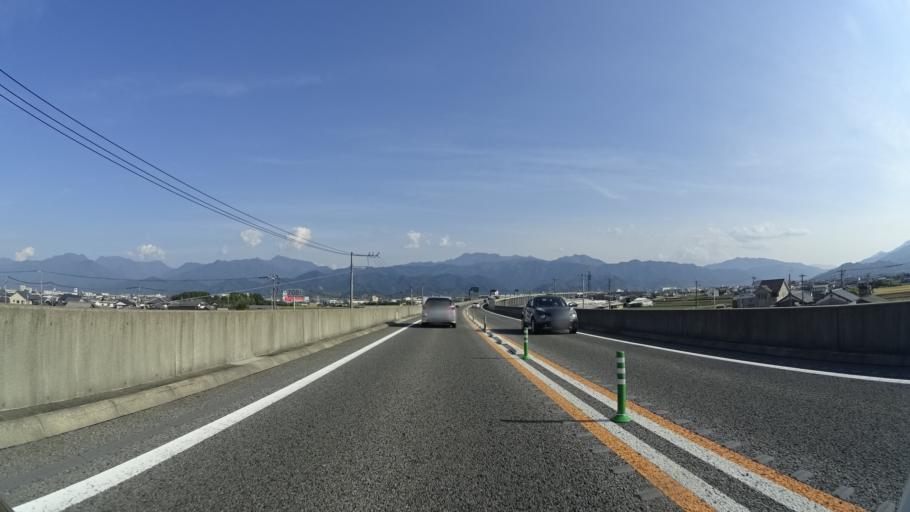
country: JP
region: Ehime
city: Saijo
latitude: 33.9265
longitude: 133.0737
